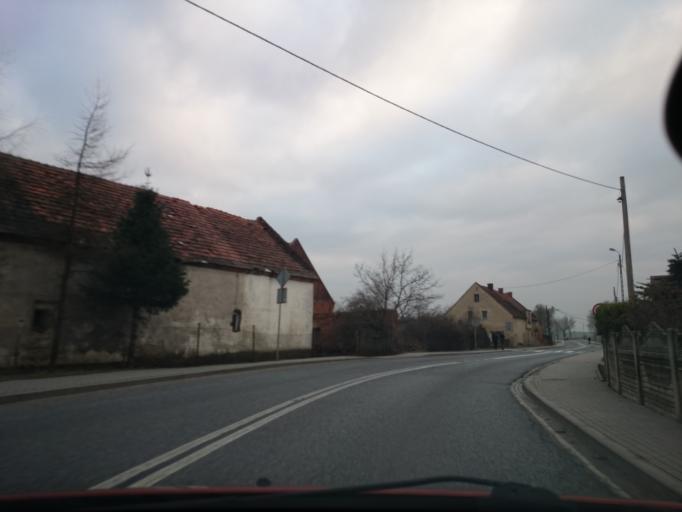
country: PL
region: Opole Voivodeship
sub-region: Powiat nyski
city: Sidzina
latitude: 50.5727
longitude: 17.4484
